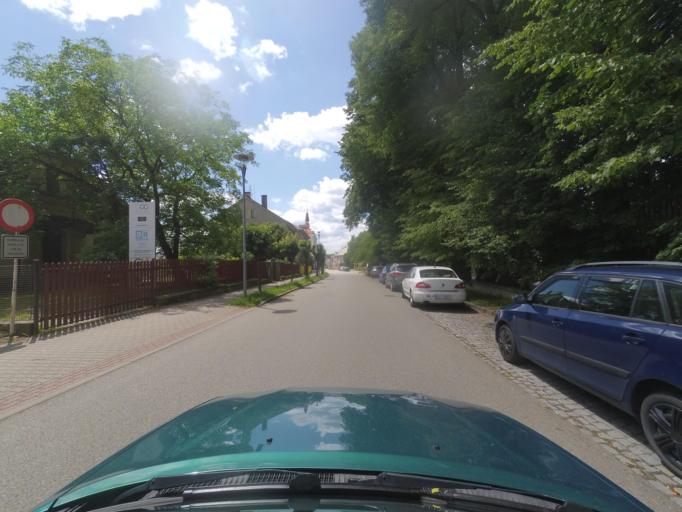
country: CZ
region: Kralovehradecky
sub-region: Okres Rychnov nad Kneznou
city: Rychnov nad Kneznou
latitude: 50.1662
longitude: 16.2795
